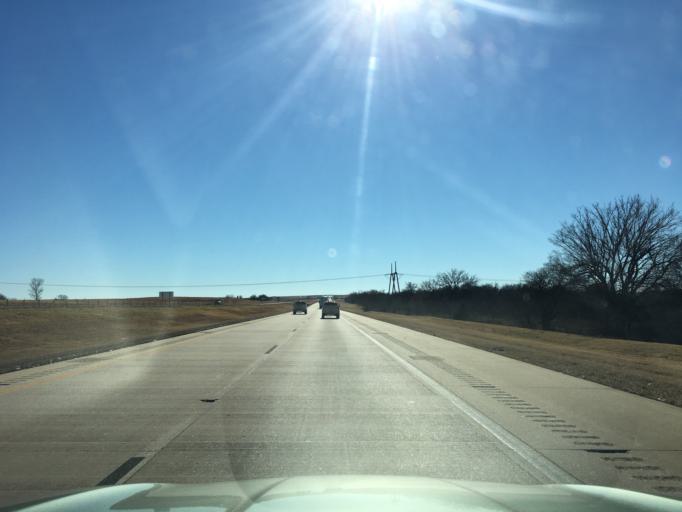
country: US
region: Oklahoma
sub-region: Noble County
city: Perry
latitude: 36.4265
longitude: -97.3272
